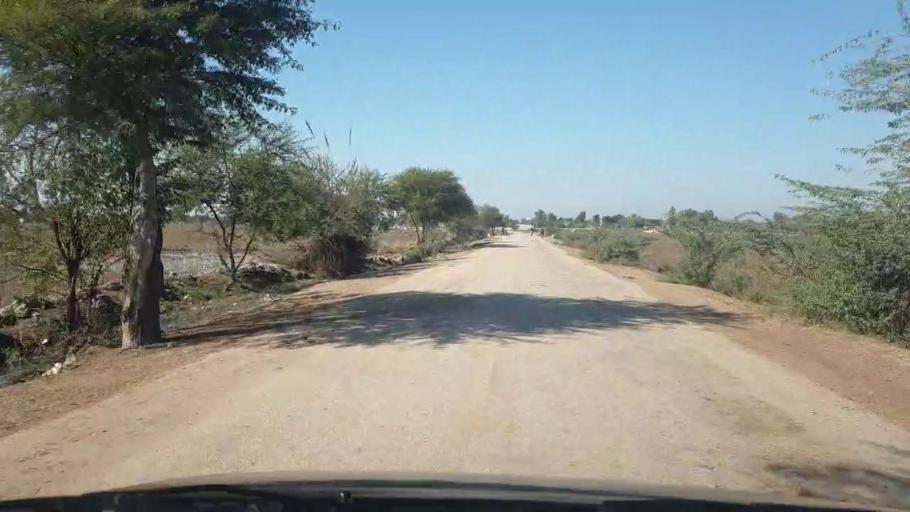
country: PK
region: Sindh
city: Bozdar
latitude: 27.1278
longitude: 68.6393
